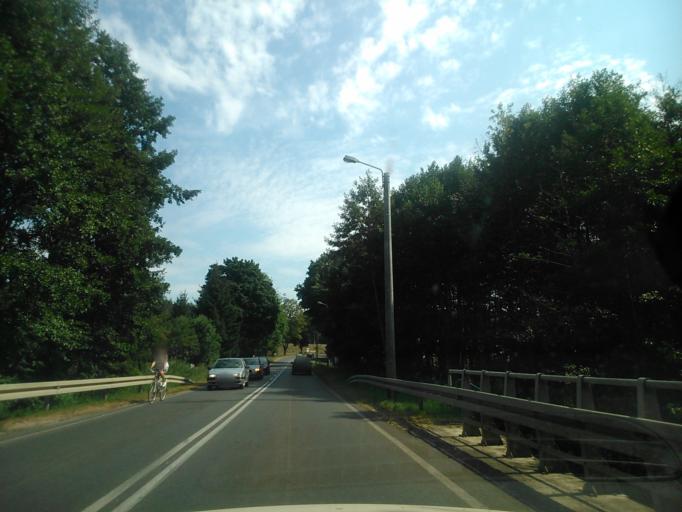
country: PL
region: Warmian-Masurian Voivodeship
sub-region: Powiat dzialdowski
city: Ilowo -Osada
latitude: 53.1479
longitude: 20.3349
